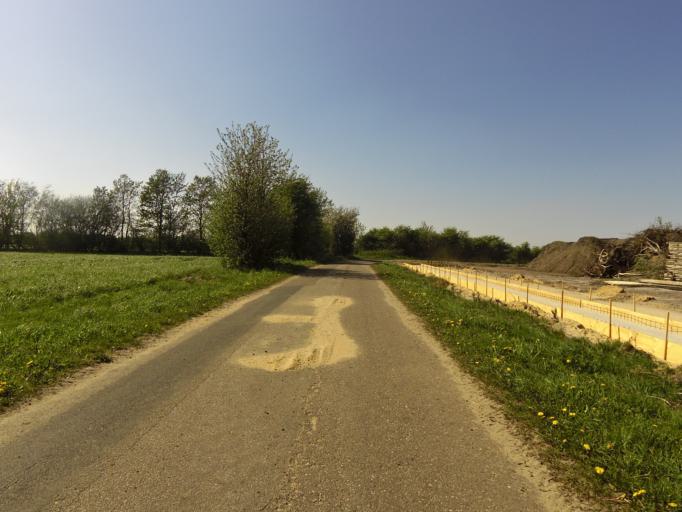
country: DK
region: South Denmark
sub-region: Tonder Kommune
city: Sherrebek
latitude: 55.2129
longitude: 8.8411
